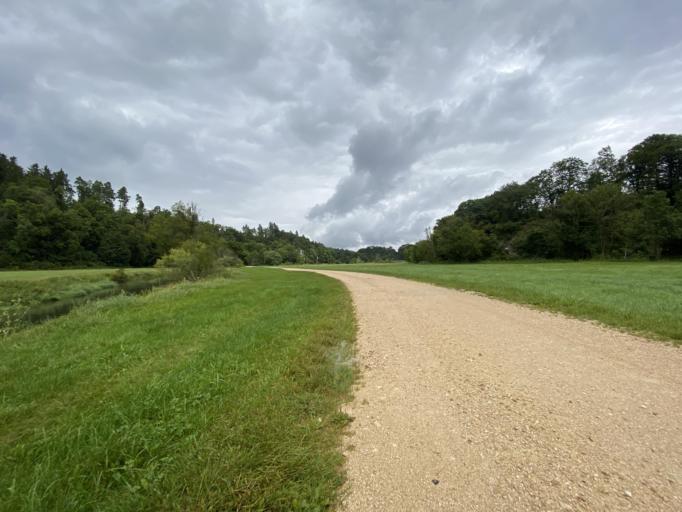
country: DE
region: Baden-Wuerttemberg
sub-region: Tuebingen Region
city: Sigmaringen
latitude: 48.1034
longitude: 9.2468
